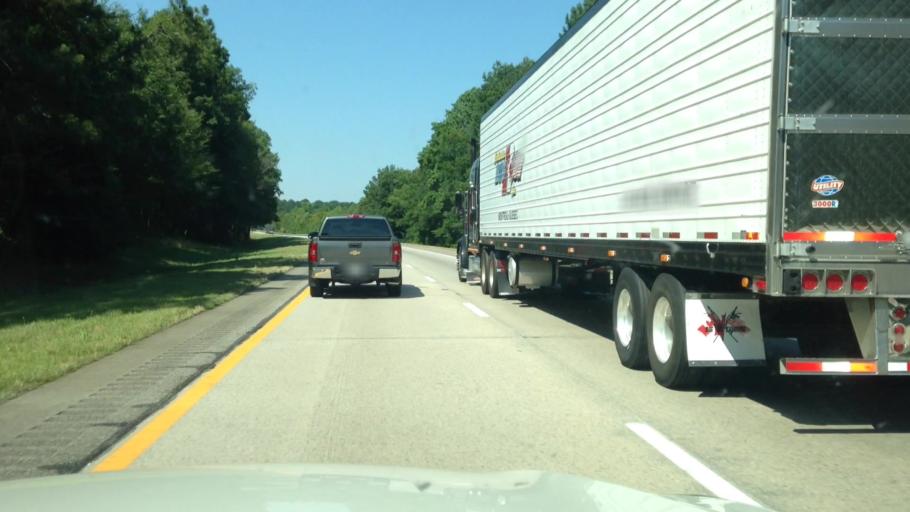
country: US
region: North Carolina
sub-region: Nash County
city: Nashville
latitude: 35.8933
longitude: -77.9336
